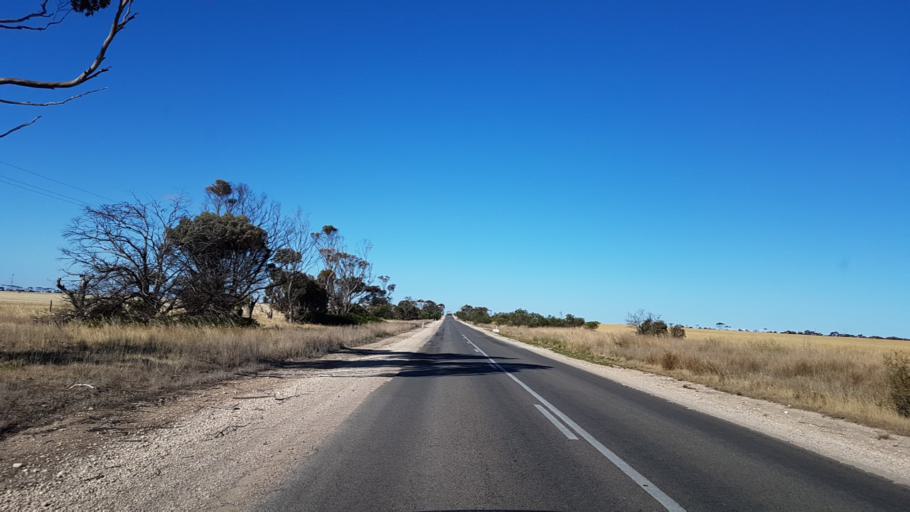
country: AU
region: South Australia
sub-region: Yorke Peninsula
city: Port Victoria
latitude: -34.7993
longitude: 137.5821
